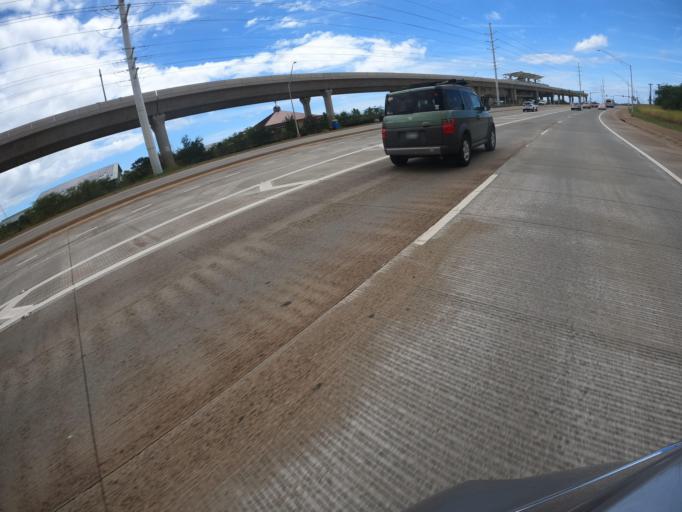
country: US
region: Hawaii
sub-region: Honolulu County
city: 'Ewa Villages
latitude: 21.3472
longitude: -158.0506
